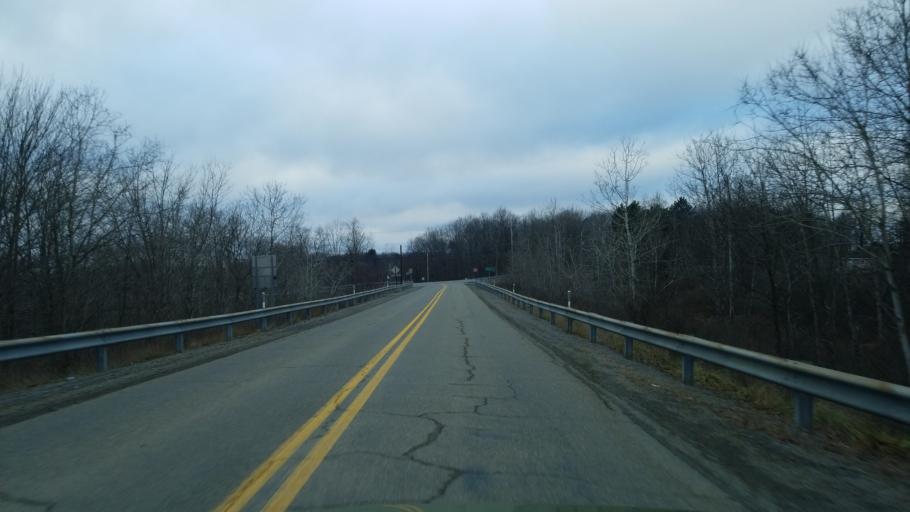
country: US
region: Pennsylvania
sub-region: Jefferson County
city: Falls Creek
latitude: 41.1590
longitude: -78.8229
